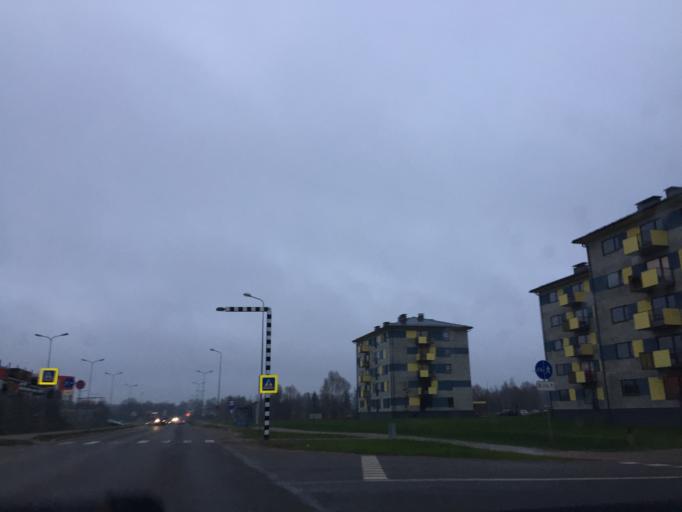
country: LV
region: Valmieras Rajons
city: Valmiera
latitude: 57.5418
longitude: 25.3960
